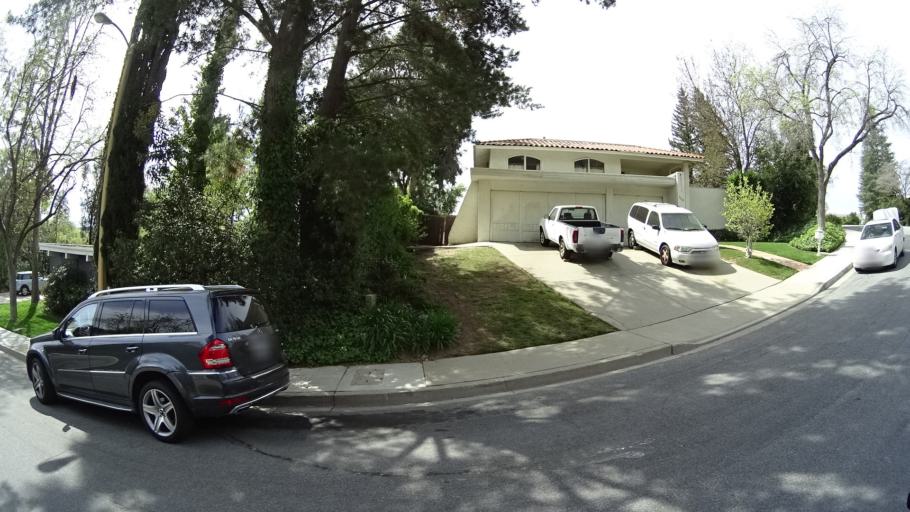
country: US
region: California
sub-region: Ventura County
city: Thousand Oaks
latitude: 34.1509
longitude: -118.8481
